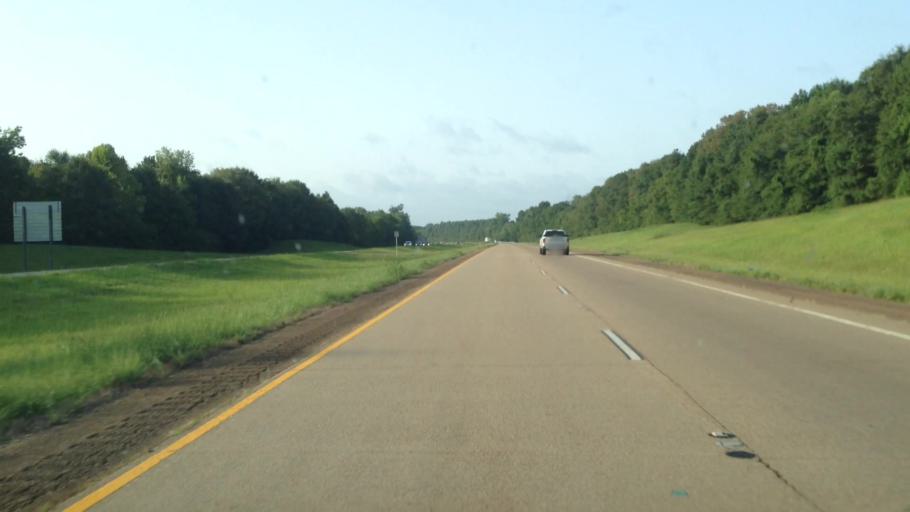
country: US
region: Louisiana
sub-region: Rapides Parish
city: Woodworth
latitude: 31.1497
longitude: -92.4534
